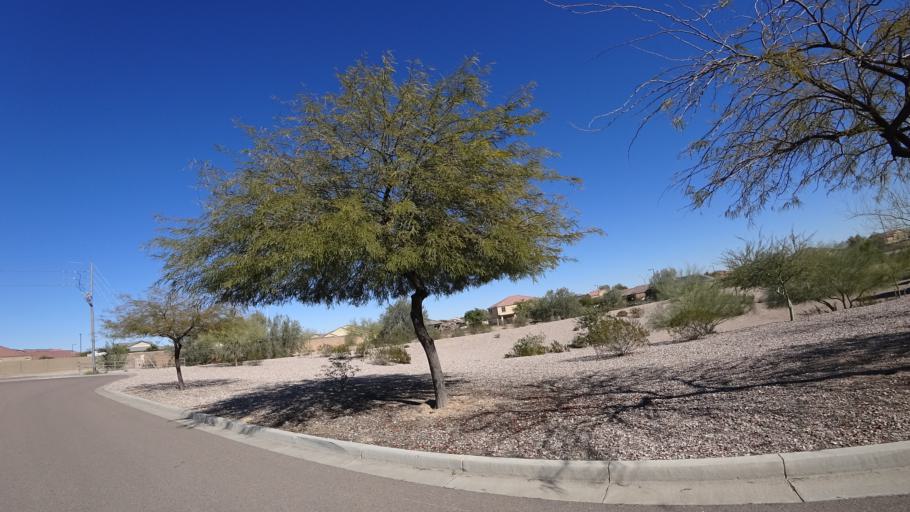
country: US
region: Arizona
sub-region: Maricopa County
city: Buckeye
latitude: 33.4280
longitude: -112.5217
